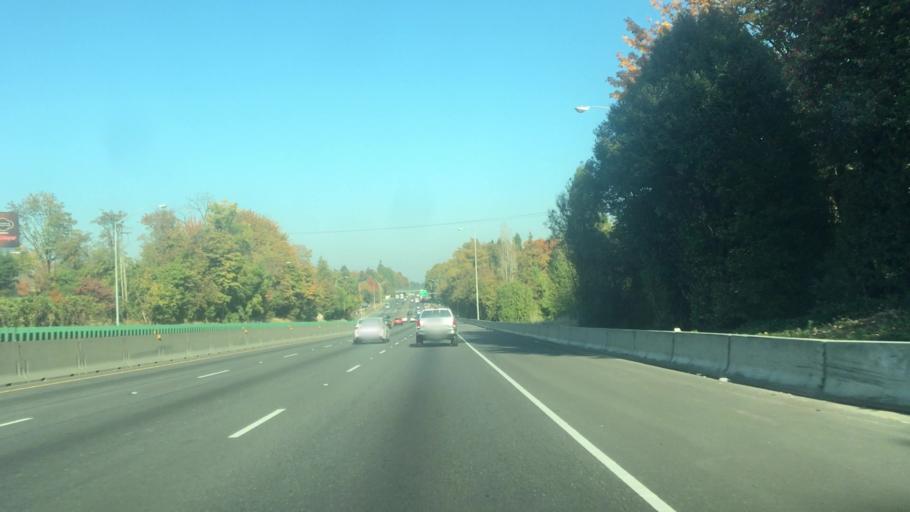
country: US
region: Oregon
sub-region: Washington County
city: Garden Home-Whitford
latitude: 45.4580
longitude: -122.7086
